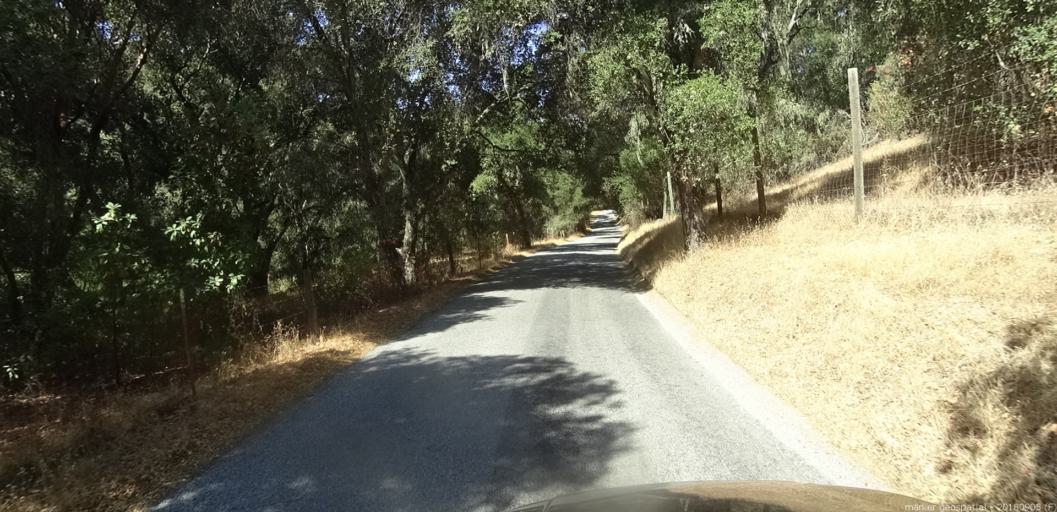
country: US
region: California
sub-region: Monterey County
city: Carmel Valley Village
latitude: 36.4089
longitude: -121.6689
